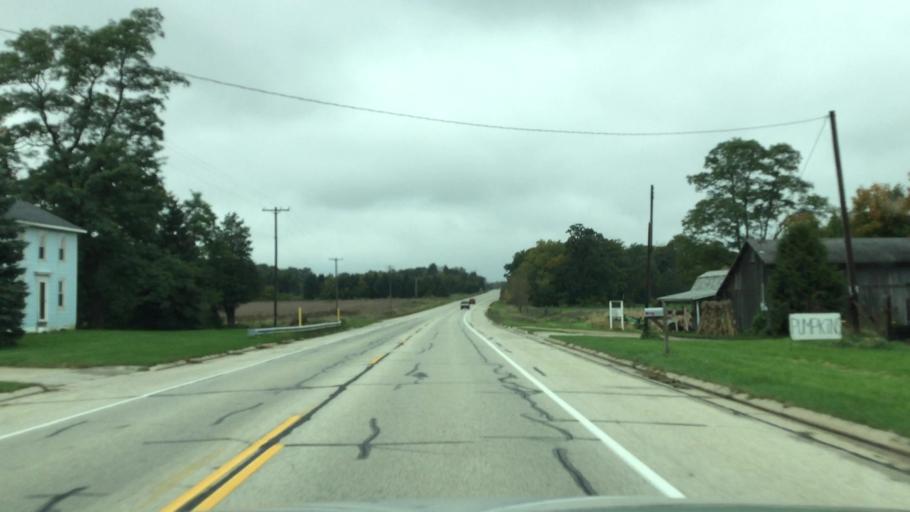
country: US
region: Wisconsin
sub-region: Racine County
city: Eagle Lake
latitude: 42.7413
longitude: -88.1255
